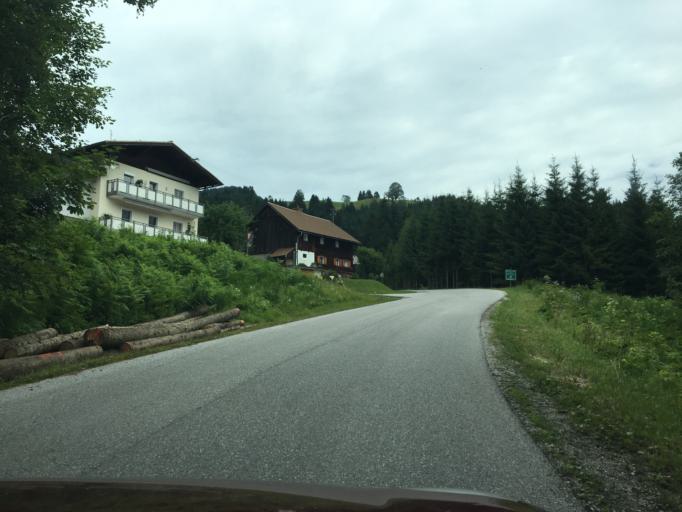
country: AT
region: Salzburg
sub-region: Politischer Bezirk Hallein
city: Abtenau
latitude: 47.6042
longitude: 13.3604
